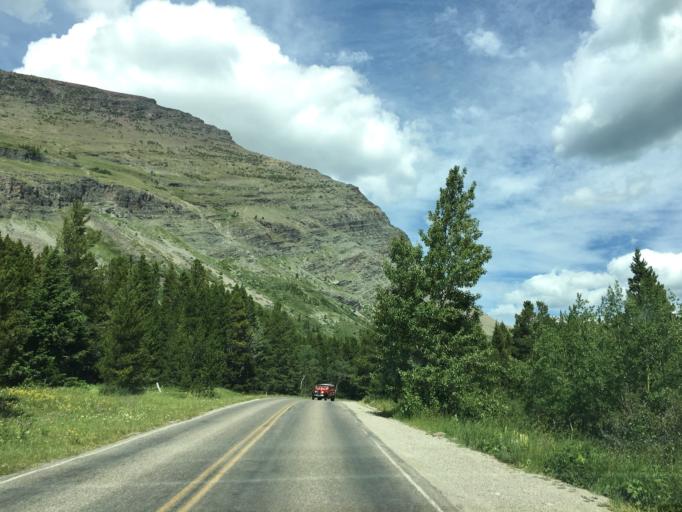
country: CA
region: Alberta
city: Cardston
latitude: 48.7985
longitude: -113.6673
